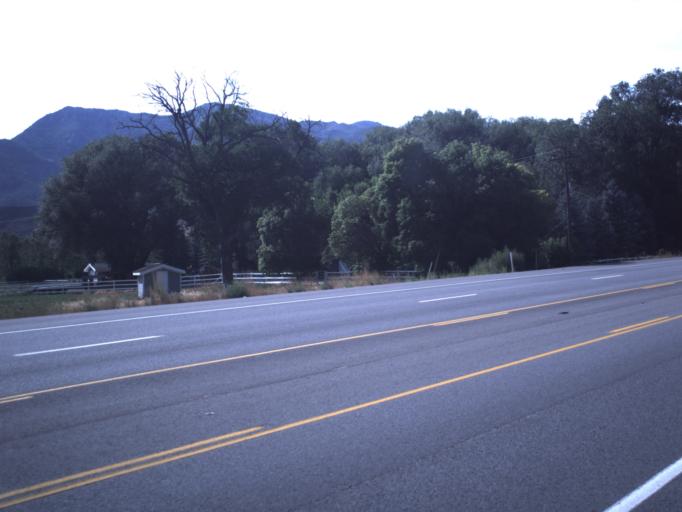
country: US
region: Utah
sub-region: Wasatch County
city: Heber
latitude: 40.5502
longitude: -111.4216
